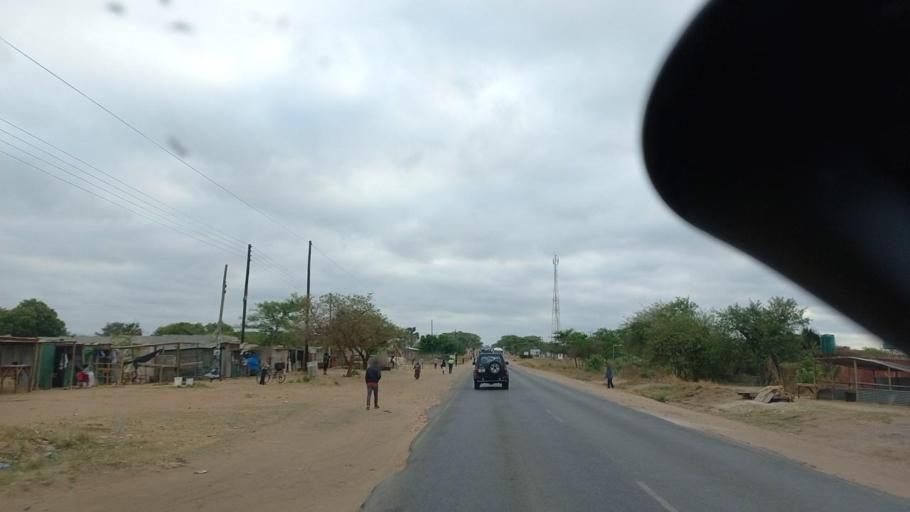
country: ZM
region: Lusaka
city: Chongwe
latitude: -15.3401
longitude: 28.6658
